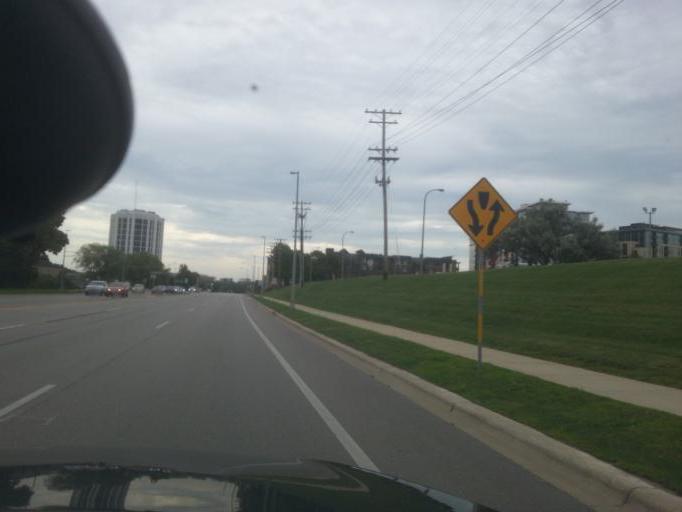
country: US
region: Wisconsin
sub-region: Dane County
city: Shorewood Hills
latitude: 43.0751
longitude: -89.4595
